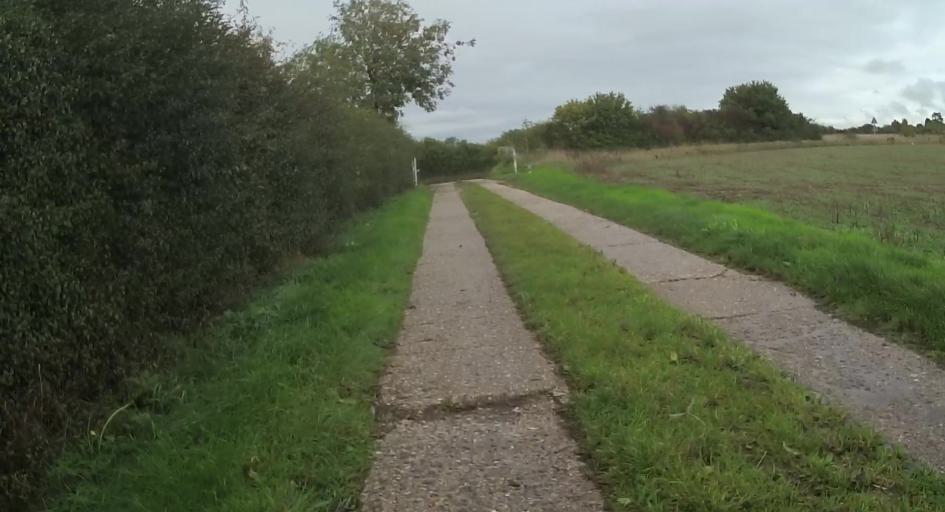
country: GB
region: England
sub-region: Hampshire
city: Basingstoke
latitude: 51.2774
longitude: -1.1348
